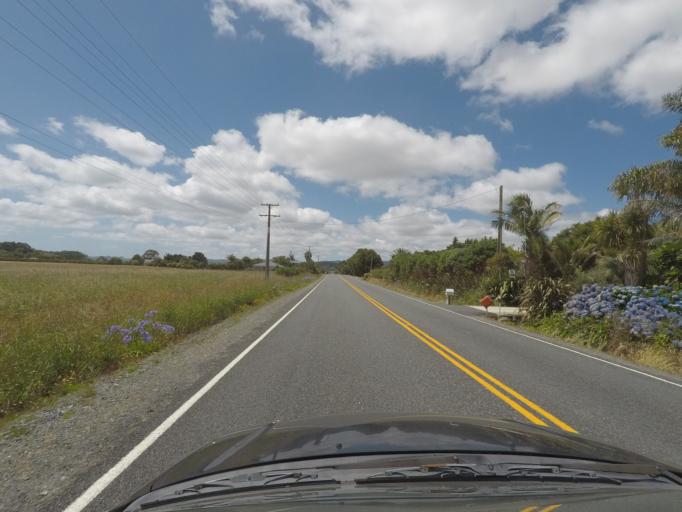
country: NZ
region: Northland
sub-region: Whangarei
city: Ruakaka
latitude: -36.0016
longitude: 174.4760
